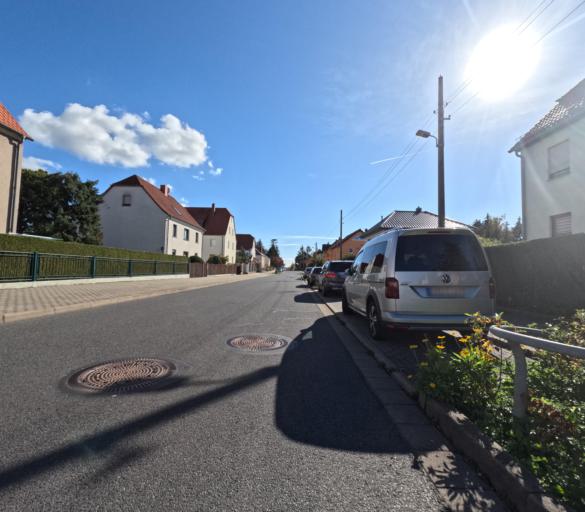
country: DE
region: Saxony
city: Albertstadt
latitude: 51.1174
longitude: 13.7242
